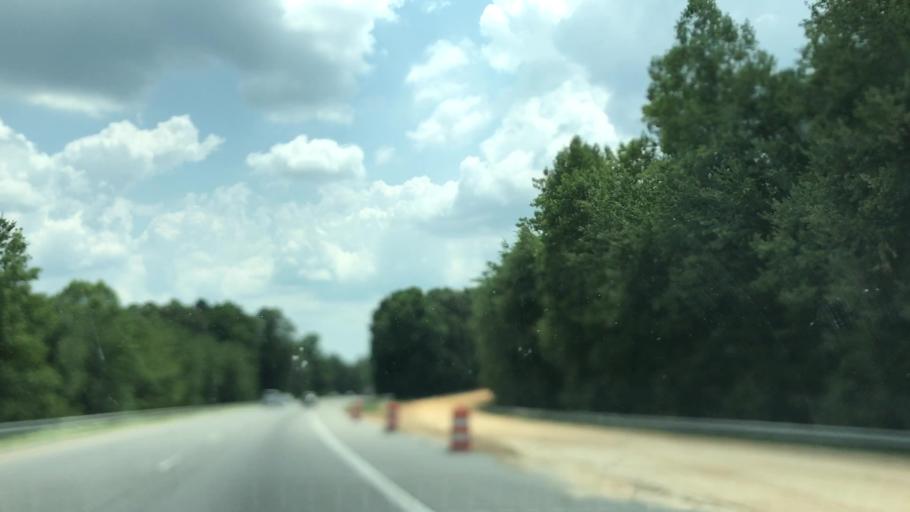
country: US
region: North Carolina
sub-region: Iredell County
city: Statesville
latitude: 35.9793
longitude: -80.8387
